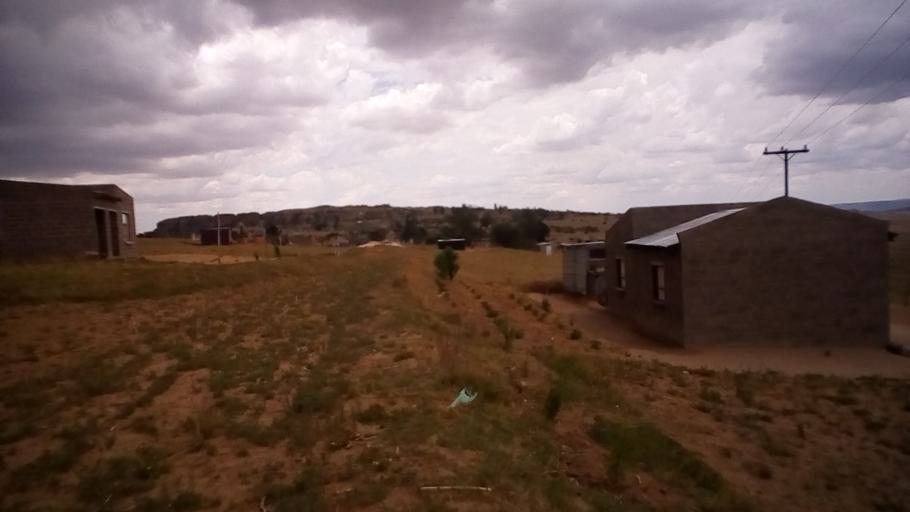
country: LS
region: Berea
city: Teyateyaneng
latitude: -29.1907
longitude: 27.8060
